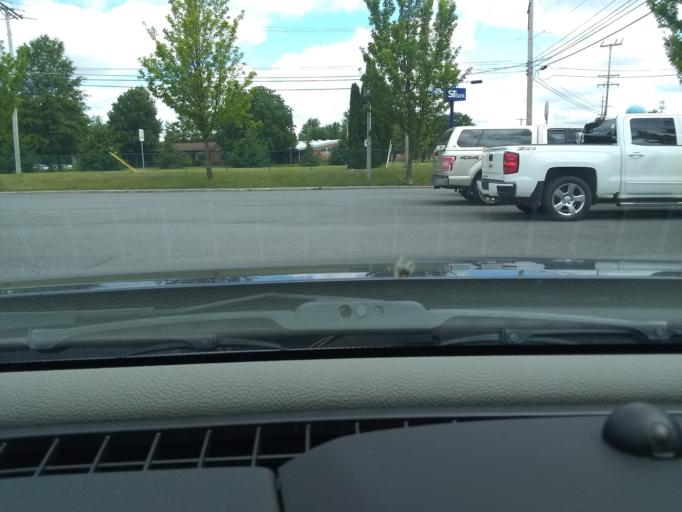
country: US
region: Pennsylvania
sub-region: Cambria County
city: Ebensburg
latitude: 40.4650
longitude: -78.7508
